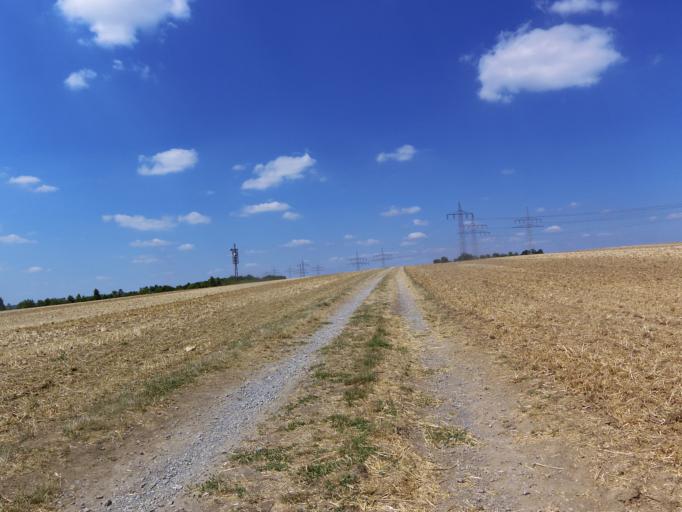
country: DE
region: Bavaria
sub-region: Regierungsbezirk Unterfranken
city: Wuerzburg
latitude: 49.8108
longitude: 9.9494
